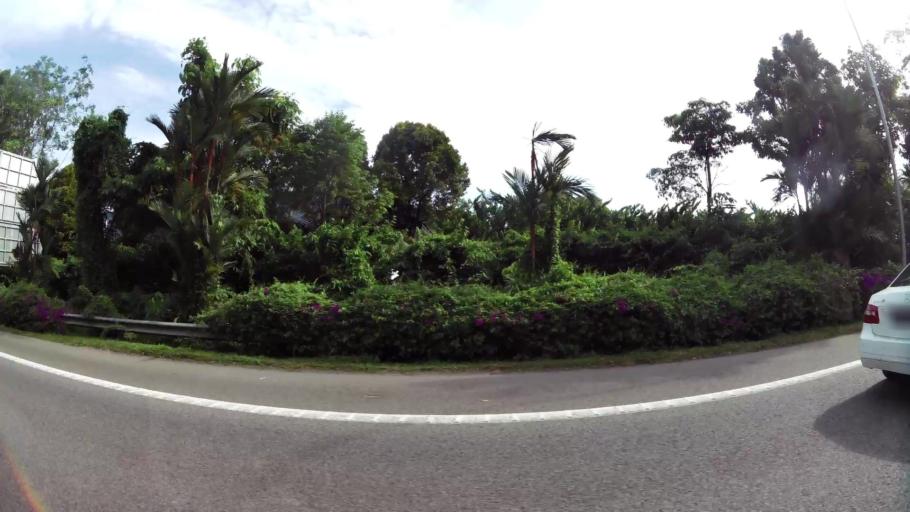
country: MY
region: Johor
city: Johor Bahru
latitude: 1.3289
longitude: 103.6575
